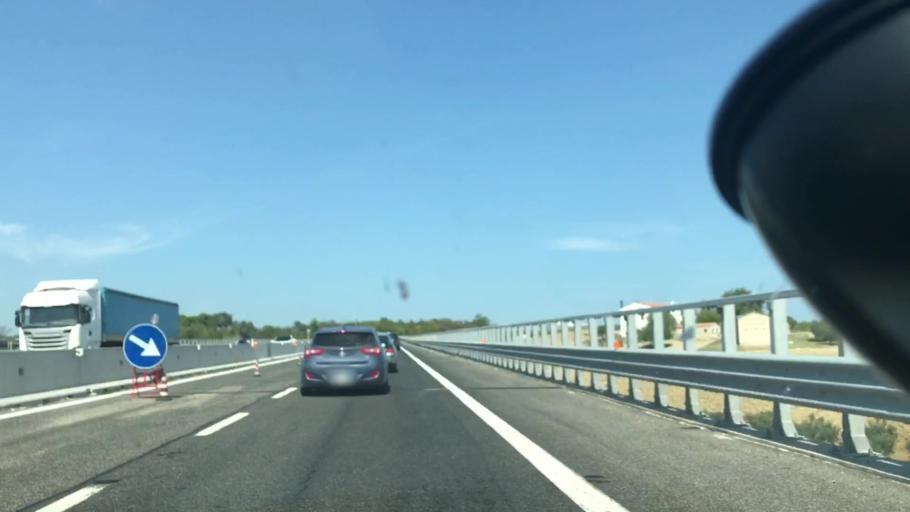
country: IT
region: Abruzzo
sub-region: Provincia di Chieti
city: Marina di Vasto
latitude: 42.0695
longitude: 14.7251
